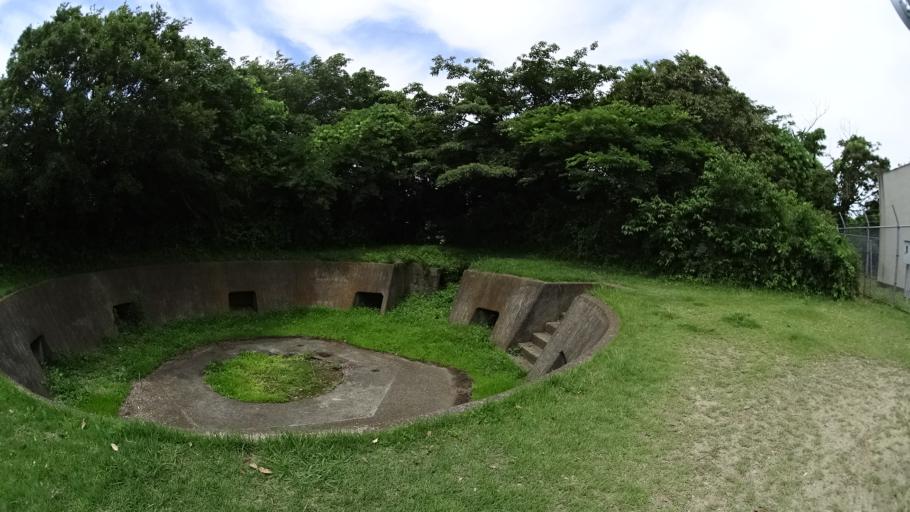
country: JP
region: Kanagawa
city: Yokosuka
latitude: 35.2191
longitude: 139.6618
